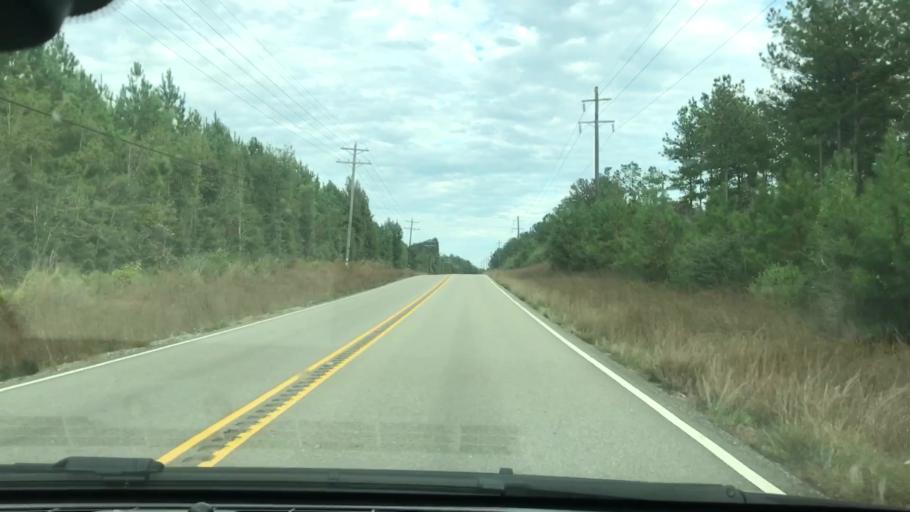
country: US
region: Louisiana
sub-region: Saint Tammany Parish
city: Abita Springs
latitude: 30.5301
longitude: -89.9129
